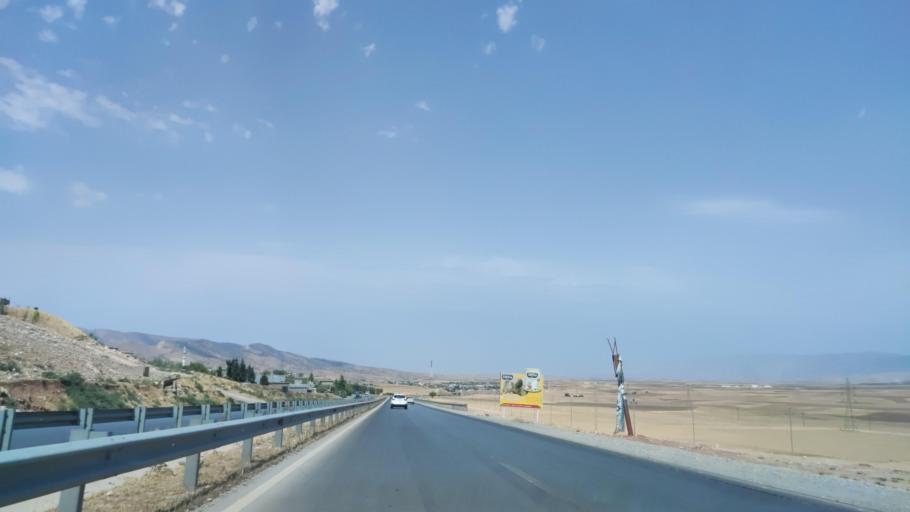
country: IQ
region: Arbil
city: Shaqlawah
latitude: 36.4910
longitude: 44.3750
